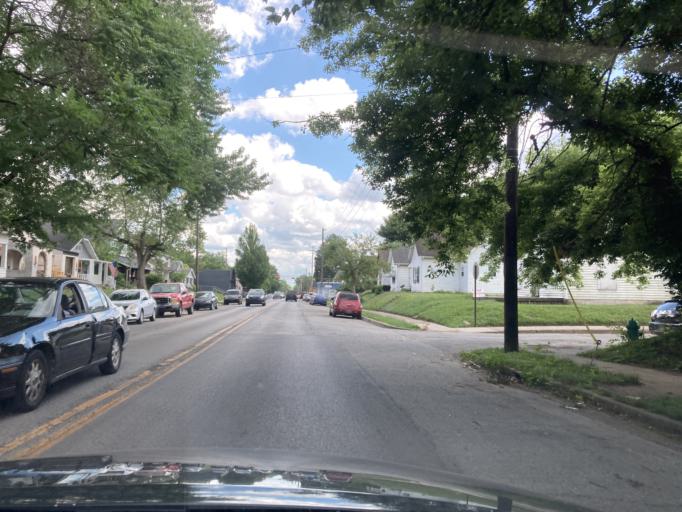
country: US
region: Indiana
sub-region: Marion County
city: Broad Ripple
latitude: 39.8296
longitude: -86.1640
